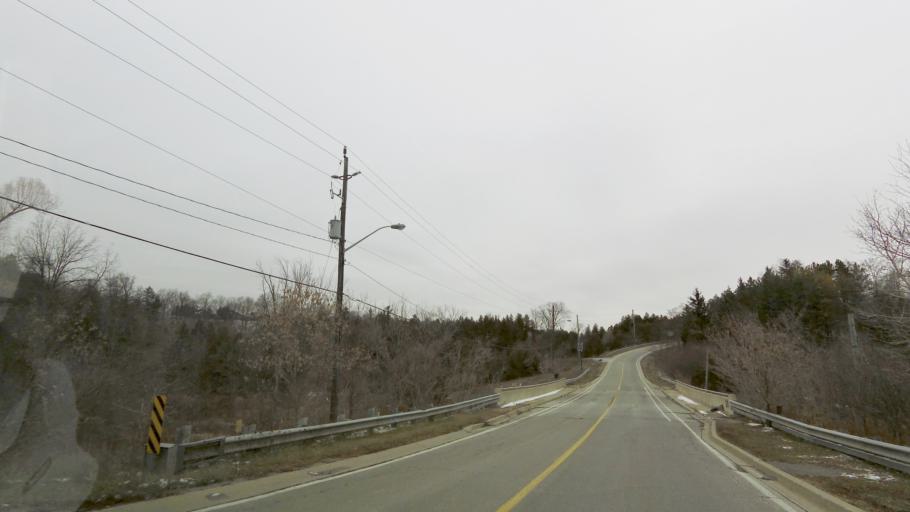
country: CA
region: Ontario
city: Vaughan
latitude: 43.8453
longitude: -79.6251
